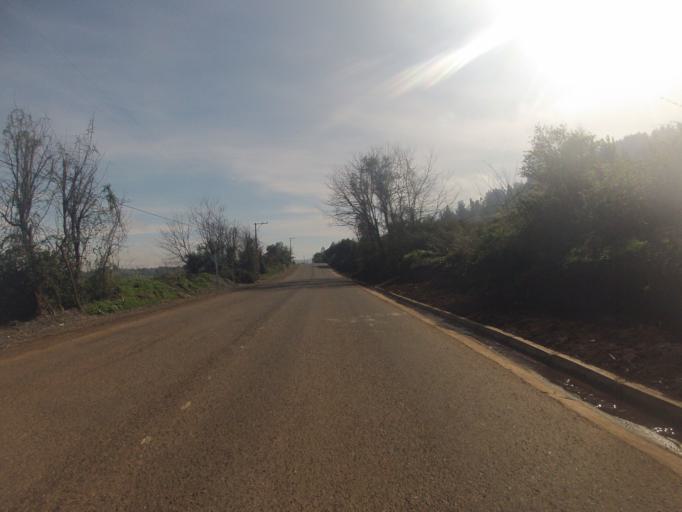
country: CL
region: Araucania
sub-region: Provincia de Cautin
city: Temuco
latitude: -38.7185
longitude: -72.5989
